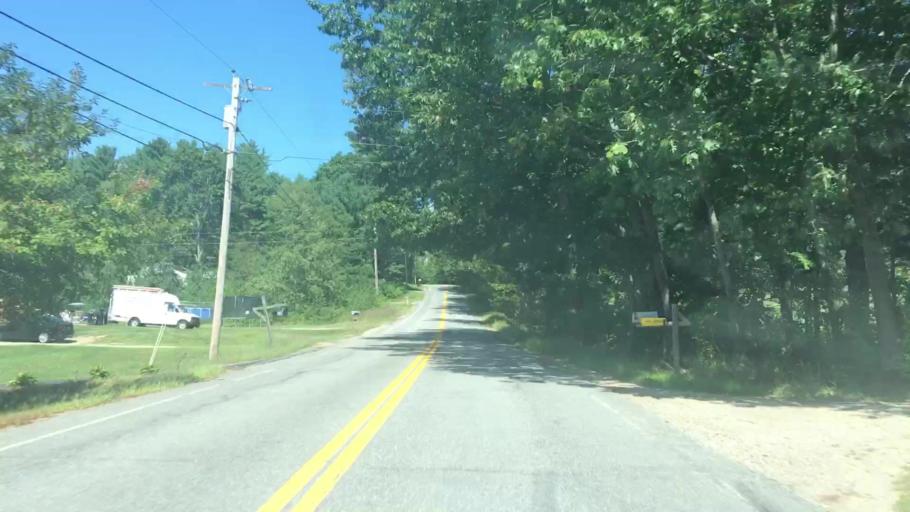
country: US
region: Maine
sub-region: Androscoggin County
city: Lisbon
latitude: 44.0568
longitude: -70.1176
